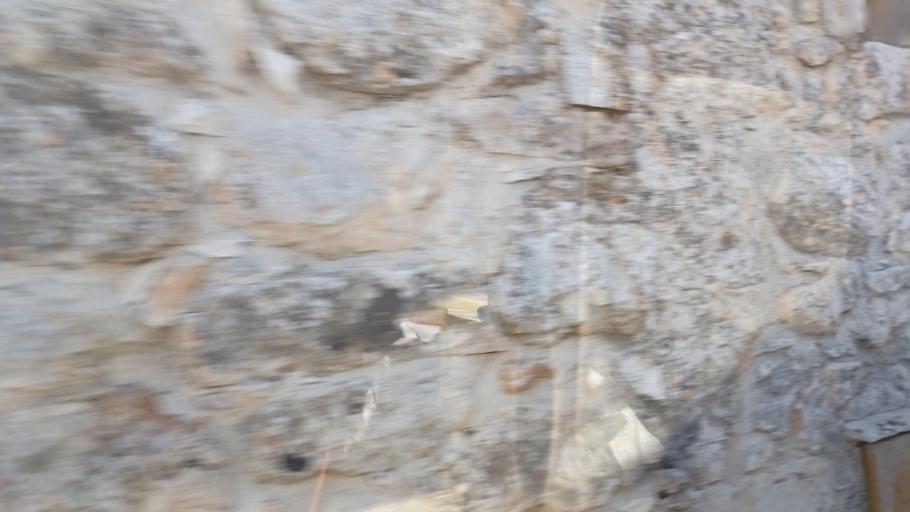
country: CY
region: Pafos
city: Pegeia
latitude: 34.9099
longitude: 32.4248
